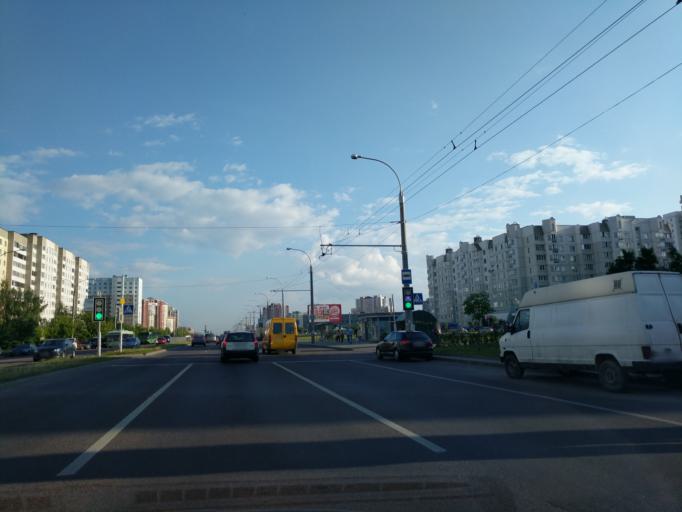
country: BY
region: Minsk
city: Novoye Medvezhino
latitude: 53.9122
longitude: 27.4363
